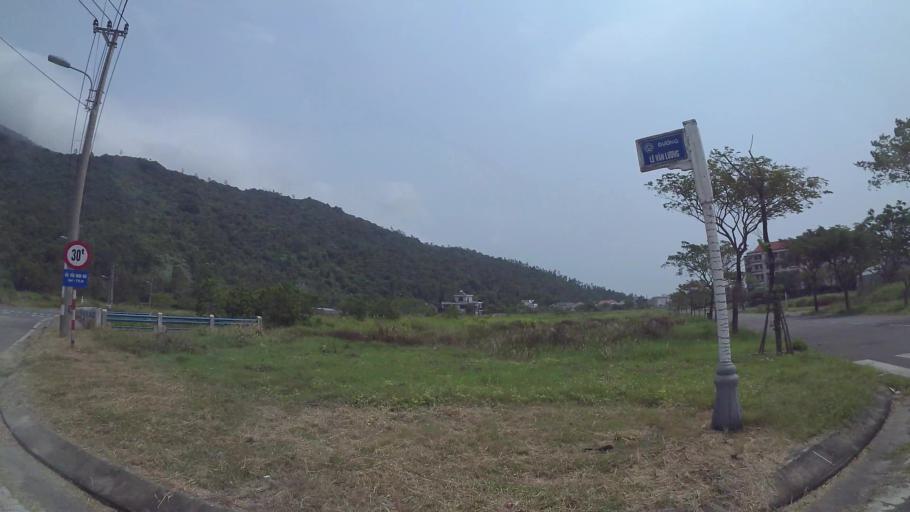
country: VN
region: Da Nang
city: Son Tra
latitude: 16.1073
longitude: 108.2613
